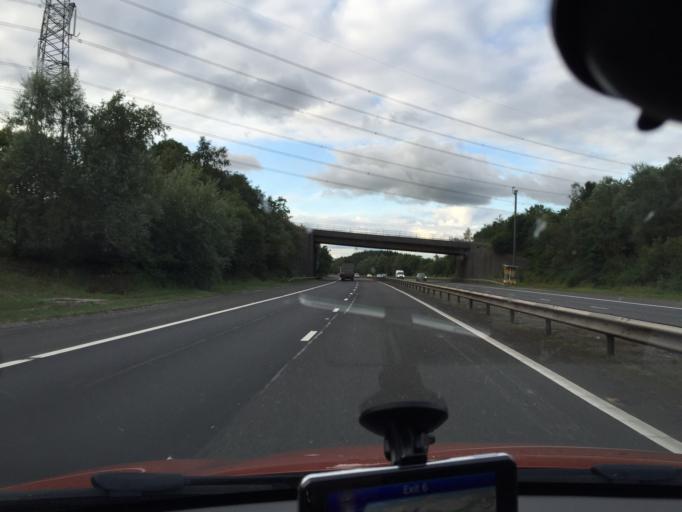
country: GB
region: Scotland
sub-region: North Lanarkshire
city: Glenboig
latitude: 55.8732
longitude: -4.0793
